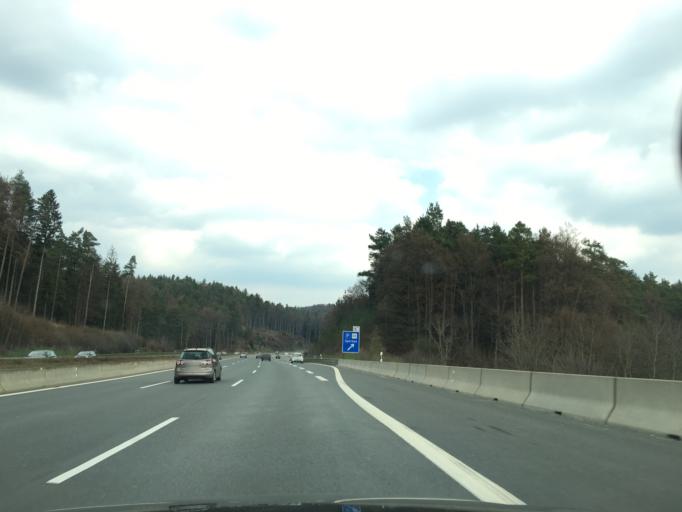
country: DE
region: Bavaria
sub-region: Regierungsbezirk Mittelfranken
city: Velden
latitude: 49.6432
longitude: 11.4336
